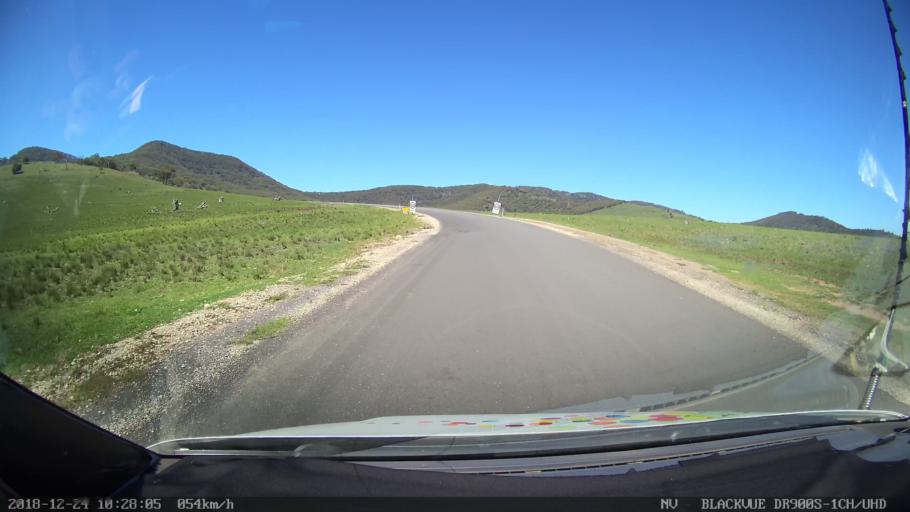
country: AU
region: New South Wales
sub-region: Liverpool Plains
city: Quirindi
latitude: -31.8247
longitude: 150.5314
